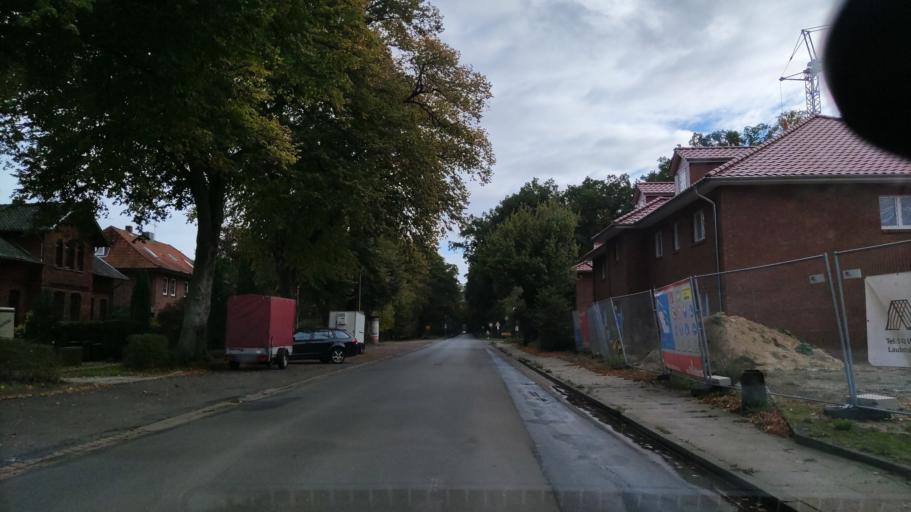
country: DE
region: Lower Saxony
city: Bad Bevensen
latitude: 53.0883
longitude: 10.5624
